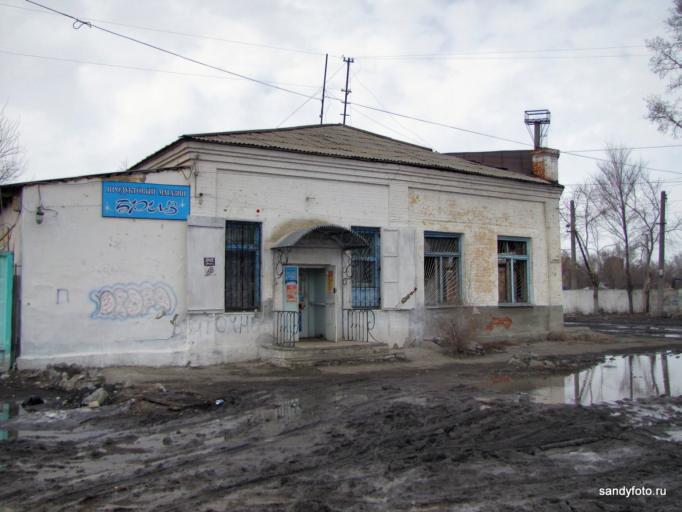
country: RU
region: Chelyabinsk
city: Troitsk
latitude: 54.1111
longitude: 61.5647
